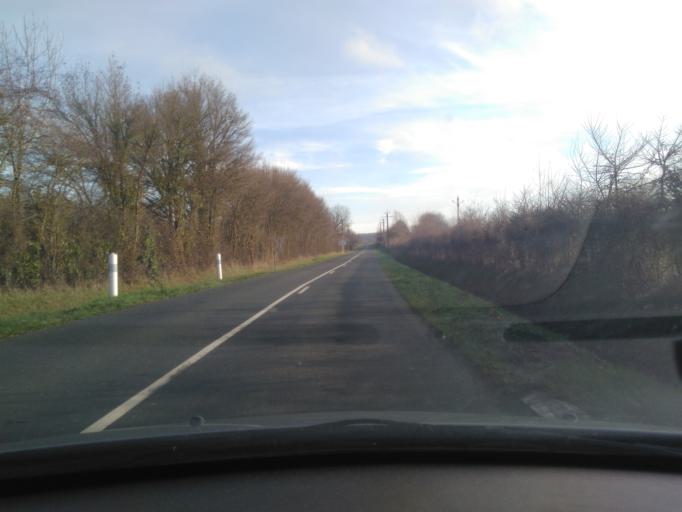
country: FR
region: Centre
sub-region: Departement de l'Indre
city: Montgivray
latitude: 46.6389
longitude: 2.0764
